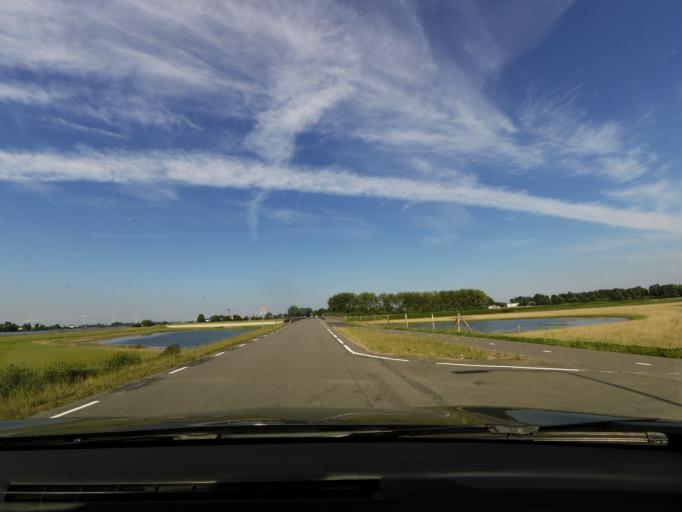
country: NL
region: South Holland
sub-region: Gemeente Hardinxveld-Giessendam
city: Neder-Hardinxveld
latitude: 51.7984
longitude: 4.8616
